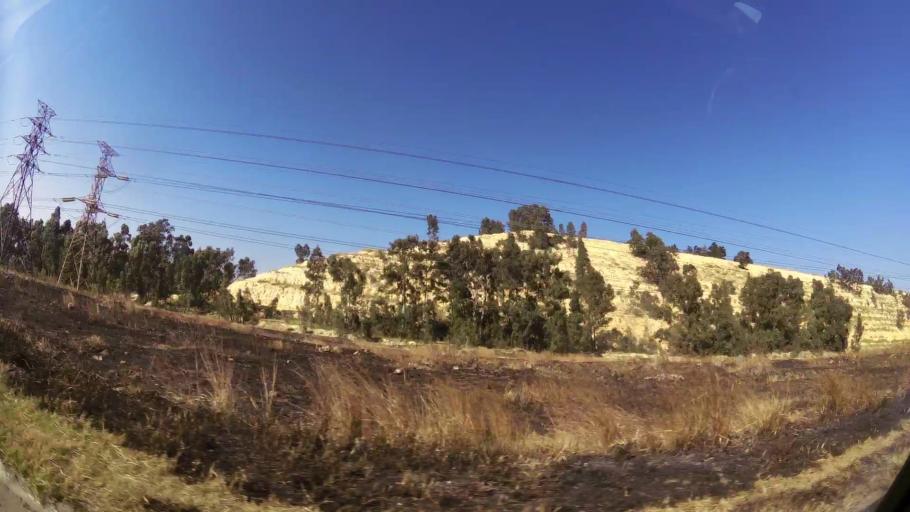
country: ZA
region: Gauteng
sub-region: City of Johannesburg Metropolitan Municipality
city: Johannesburg
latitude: -26.2277
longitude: 28.1021
